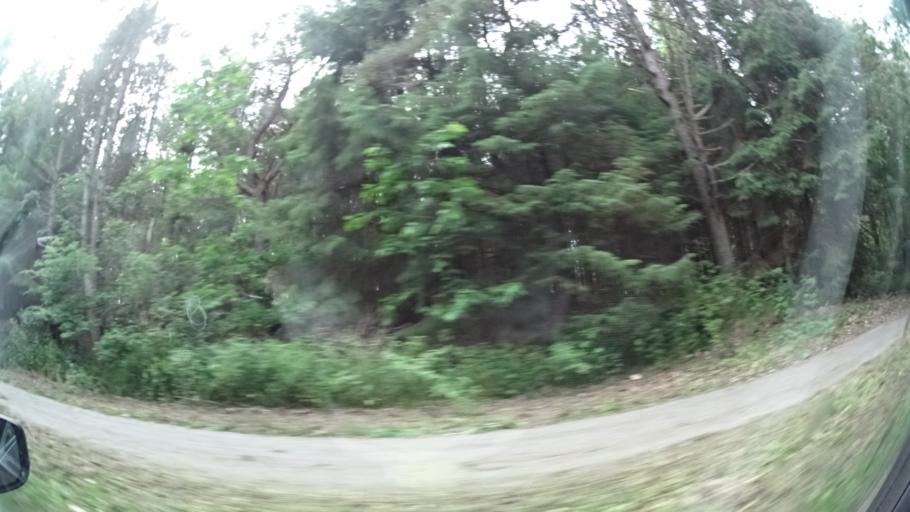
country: DK
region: Central Jutland
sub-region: Norddjurs Kommune
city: Grenaa
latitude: 56.4911
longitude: 10.7361
